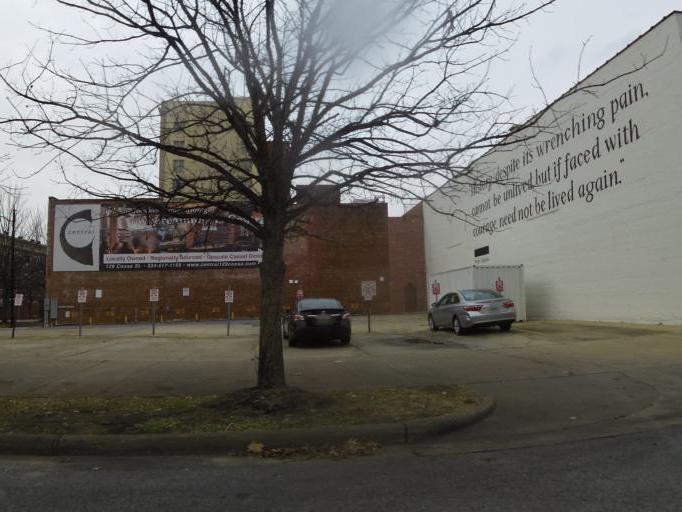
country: US
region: Alabama
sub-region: Montgomery County
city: Montgomery
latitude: 32.3799
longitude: -86.3100
